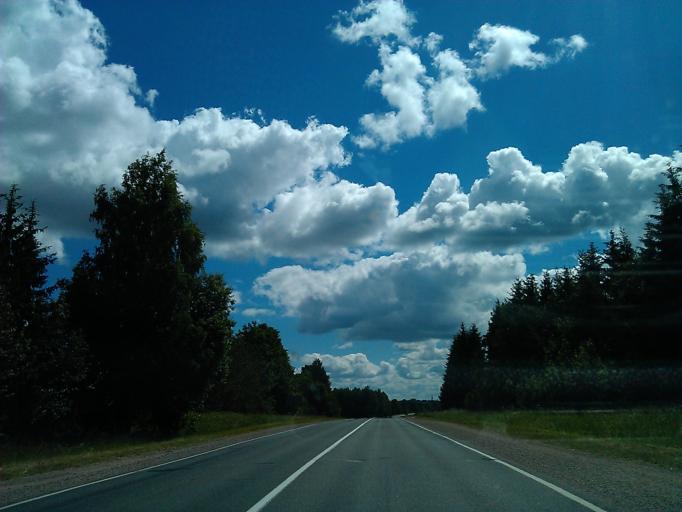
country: LV
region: Vilanu
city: Vilani
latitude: 56.5760
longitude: 26.9062
